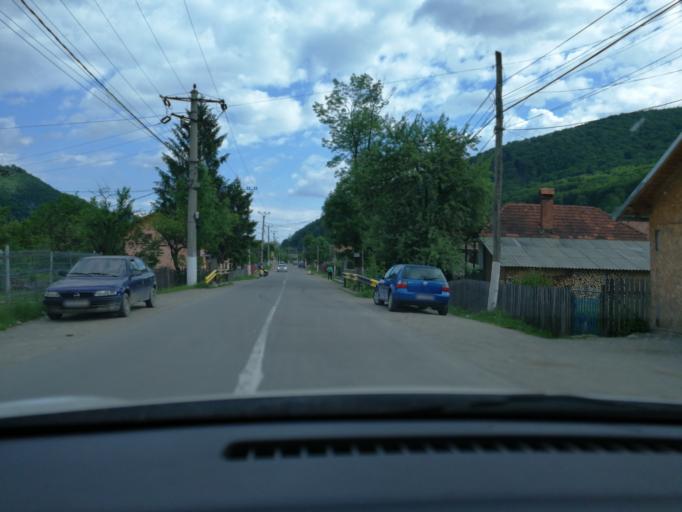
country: RO
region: Prahova
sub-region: Comuna Valea Doftanei
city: Tesila
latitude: 45.2910
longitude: 25.7226
